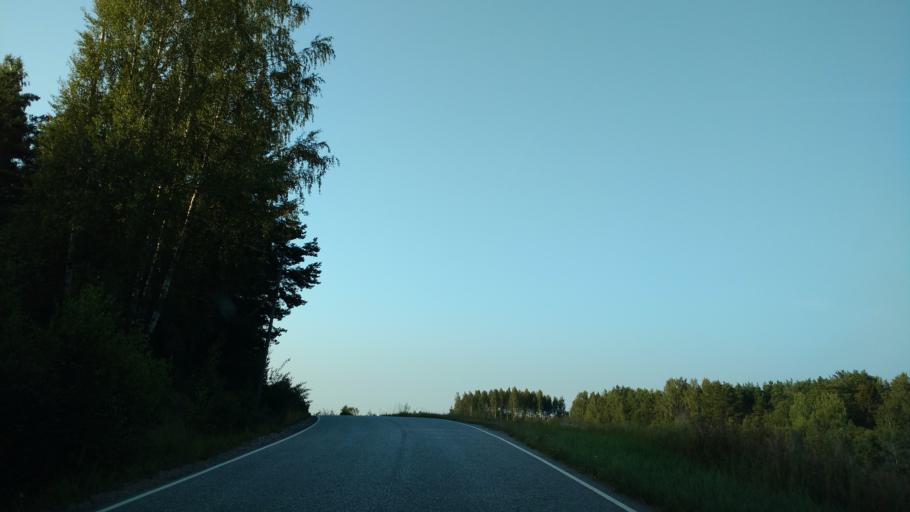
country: FI
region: Varsinais-Suomi
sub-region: Aboland-Turunmaa
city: Dragsfjaerd
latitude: 60.0460
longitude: 22.4517
